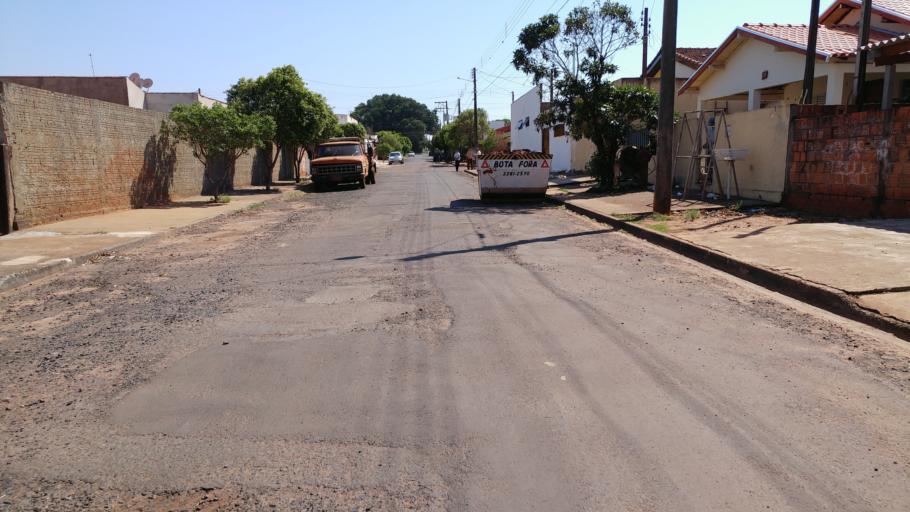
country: BR
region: Sao Paulo
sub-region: Paraguacu Paulista
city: Paraguacu Paulista
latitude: -22.4200
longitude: -50.5883
